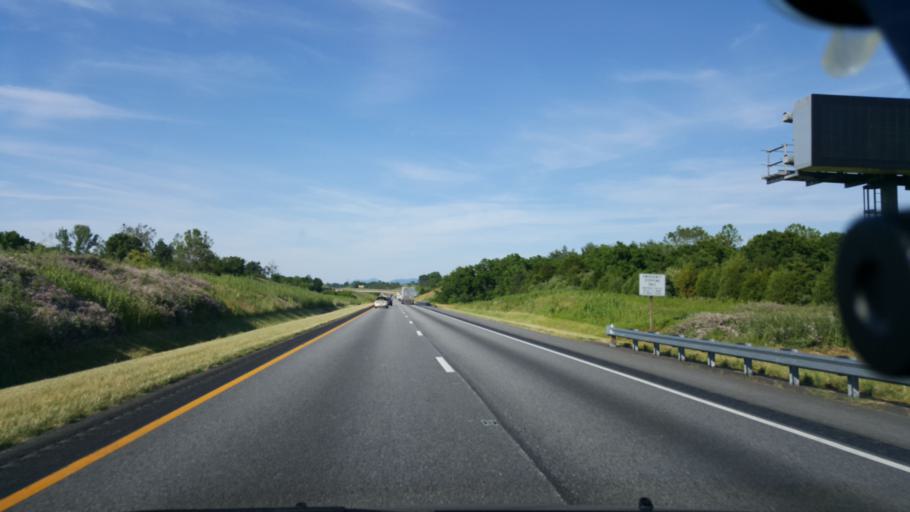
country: US
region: Virginia
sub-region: Augusta County
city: Verona
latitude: 38.2323
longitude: -78.9718
